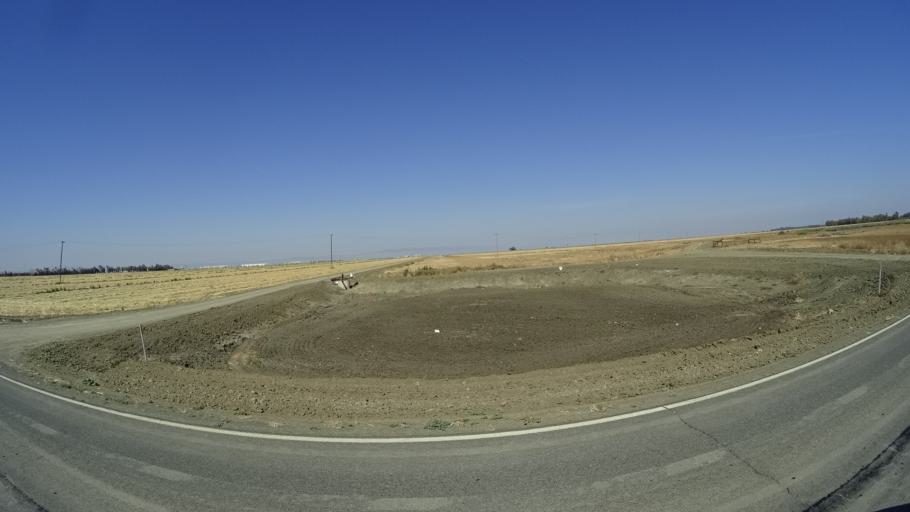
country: US
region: California
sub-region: Kings County
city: Lemoore Station
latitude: 36.3503
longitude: -119.9053
